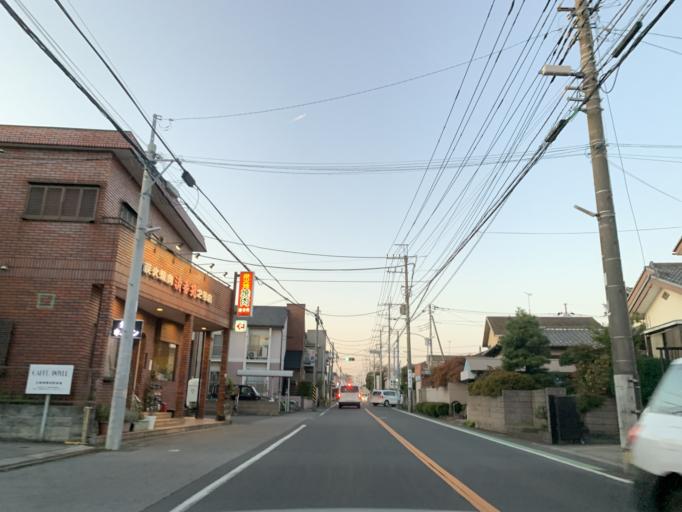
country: JP
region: Chiba
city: Nagareyama
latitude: 35.9012
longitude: 139.9067
